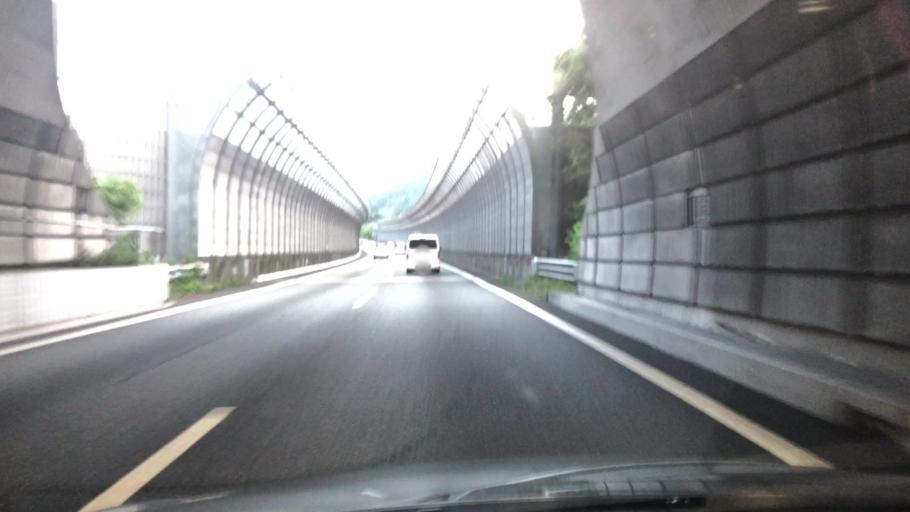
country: JP
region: Tokyo
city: Itsukaichi
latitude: 35.6871
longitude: 139.2579
